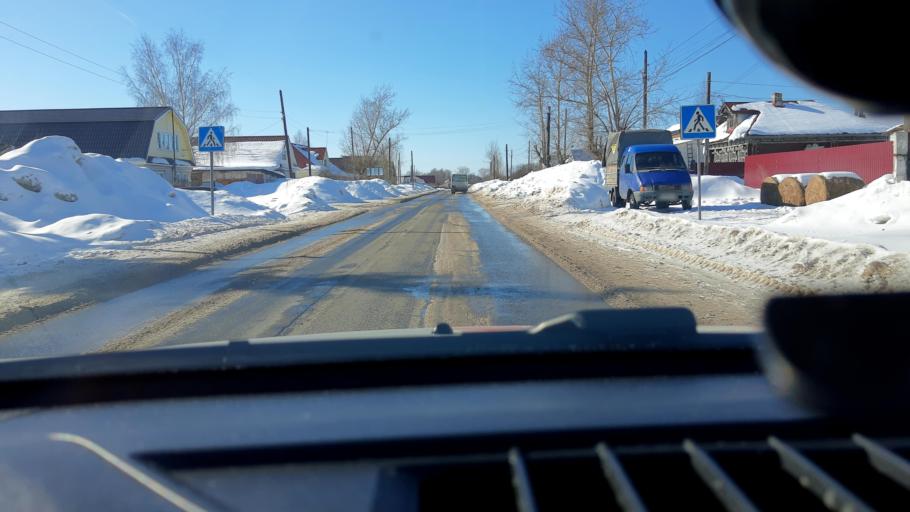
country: RU
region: Nizjnij Novgorod
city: Volodarsk
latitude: 56.2302
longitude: 43.2030
